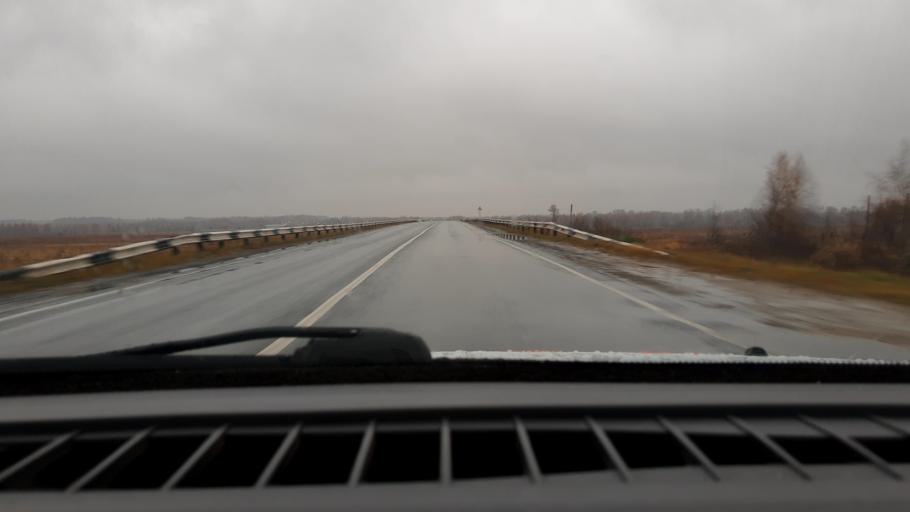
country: RU
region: Nizjnij Novgorod
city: Sitniki
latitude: 56.4926
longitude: 44.0231
